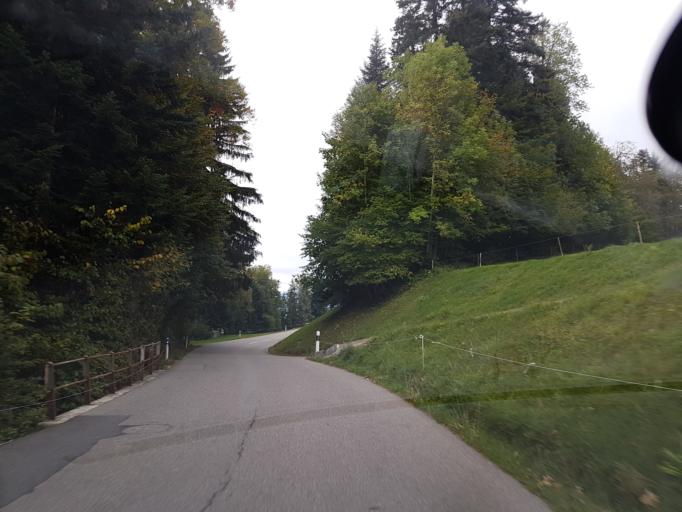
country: CH
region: Saint Gallen
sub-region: Wahlkreis See-Gaster
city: Goldingen
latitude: 47.2688
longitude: 8.9675
